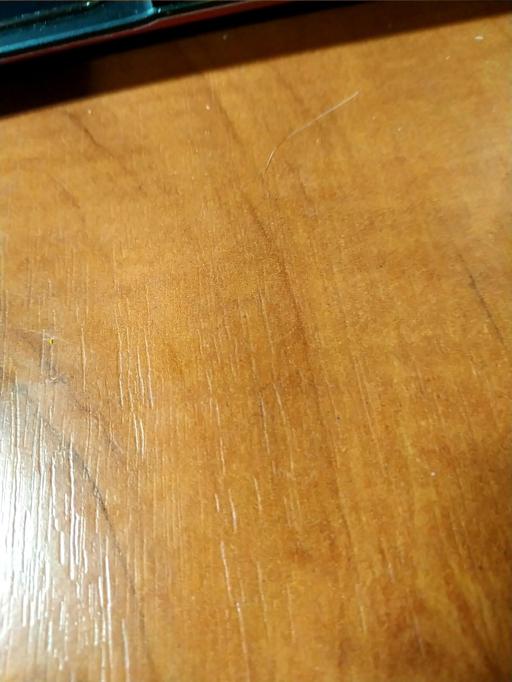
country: RU
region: Smolensk
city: Yartsevo
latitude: 55.4116
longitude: 32.8337
